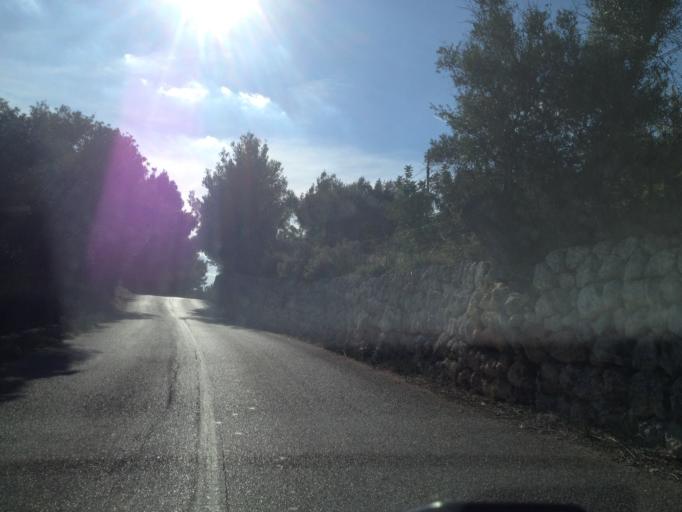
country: ES
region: Balearic Islands
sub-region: Illes Balears
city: Selva
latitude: 39.7454
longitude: 2.8988
